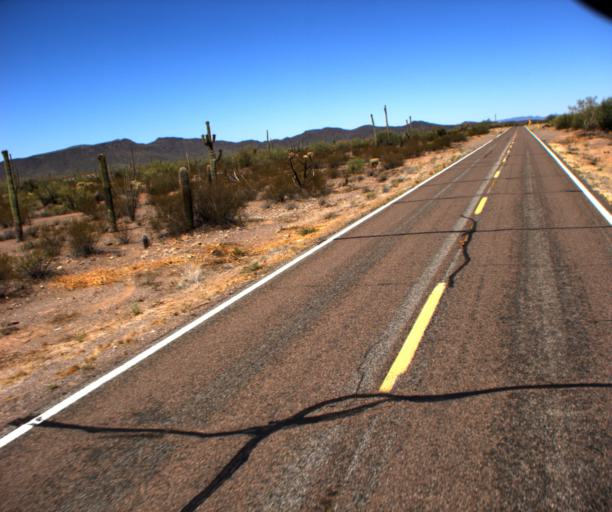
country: US
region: Arizona
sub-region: Pima County
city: Ajo
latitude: 32.2224
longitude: -112.6905
